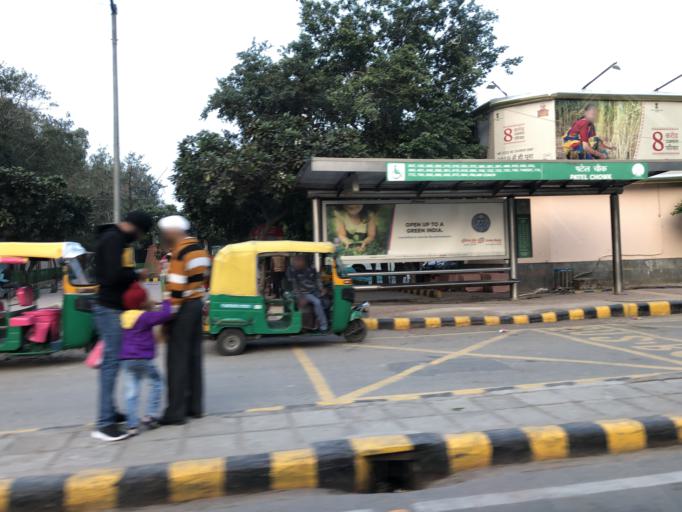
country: IN
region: NCT
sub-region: New Delhi
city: New Delhi
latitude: 28.6227
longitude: 77.2141
